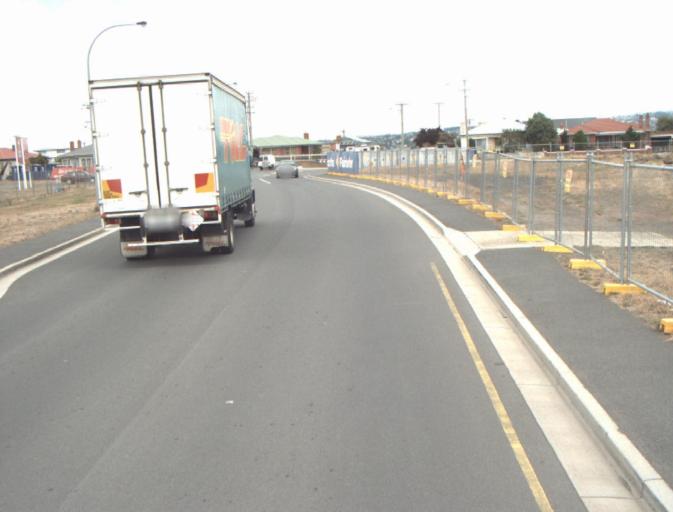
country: AU
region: Tasmania
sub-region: Launceston
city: Newnham
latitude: -41.4054
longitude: 147.1360
